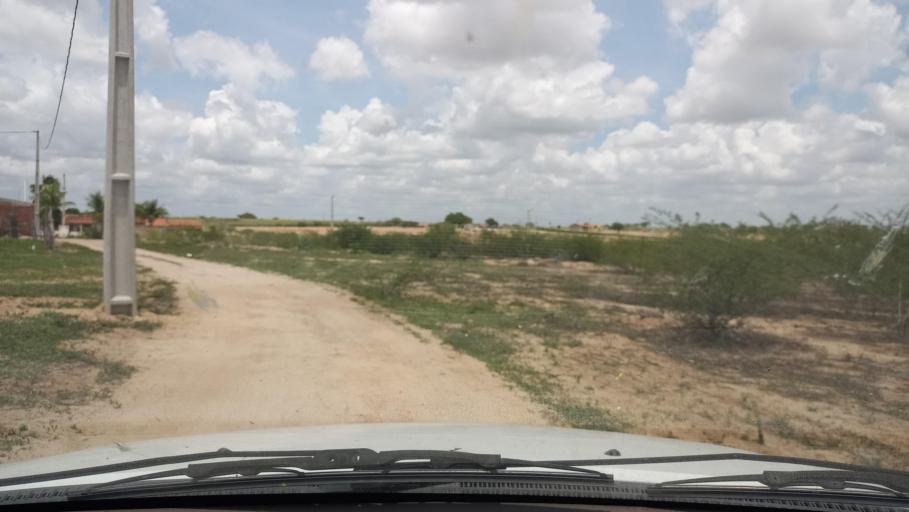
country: BR
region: Rio Grande do Norte
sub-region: Tangara
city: Tangara
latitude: -6.0946
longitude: -35.7082
